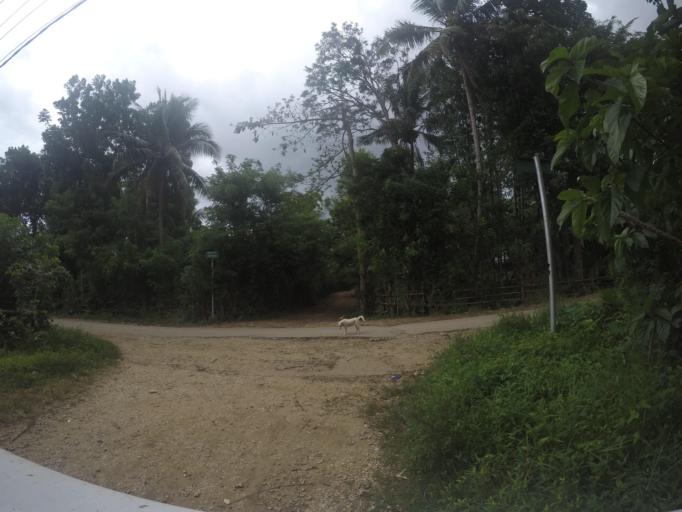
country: TL
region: Lautem
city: Lospalos
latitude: -8.5242
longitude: 126.9891
